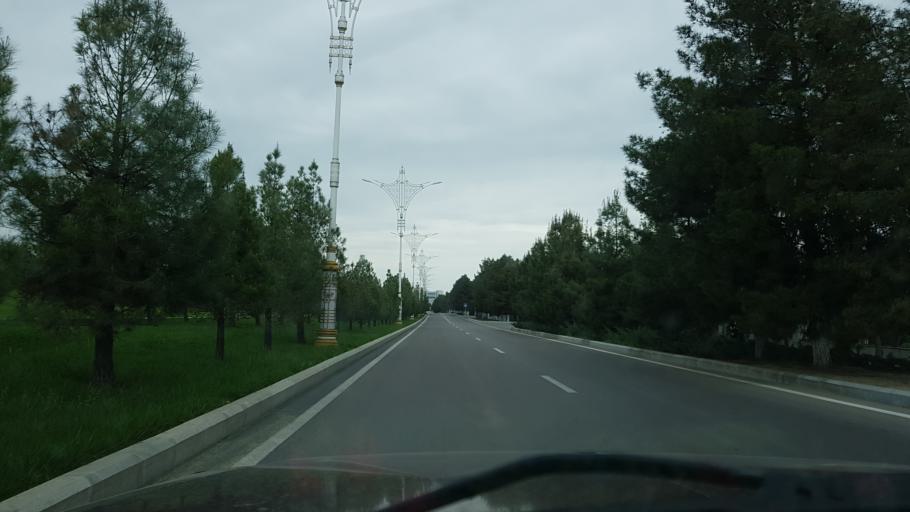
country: TM
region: Ahal
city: Ashgabat
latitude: 37.8853
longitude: 58.3582
